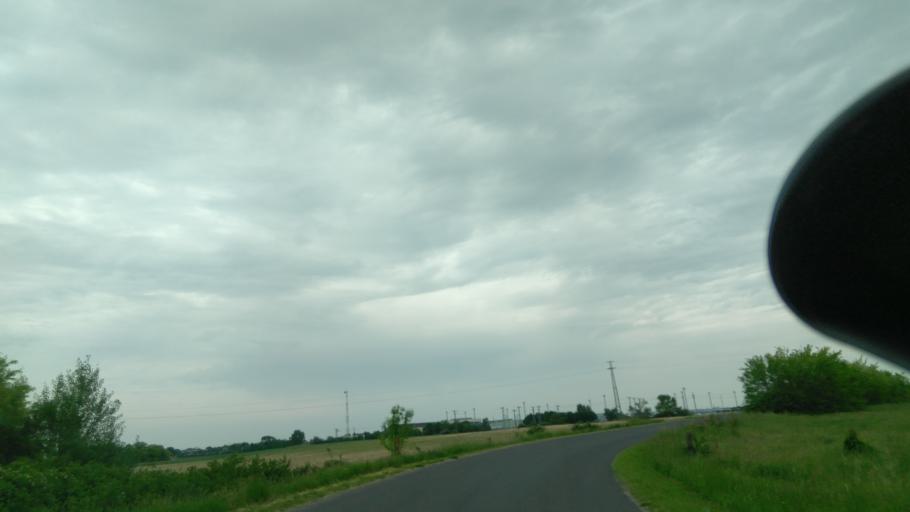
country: HU
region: Bekes
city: Fuzesgyarmat
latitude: 47.0886
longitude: 21.2060
